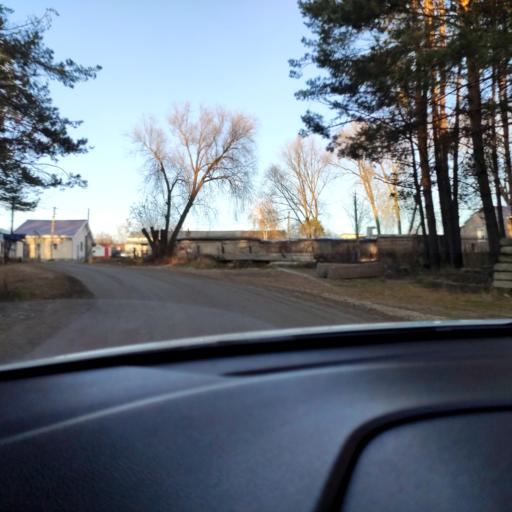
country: RU
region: Tatarstan
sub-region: Gorod Kazan'
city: Kazan
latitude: 55.8877
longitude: 49.0565
